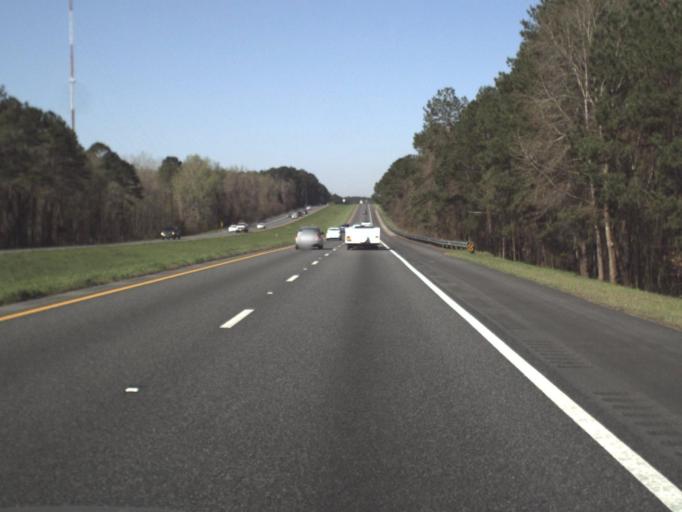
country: US
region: Florida
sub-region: Leon County
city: Tallahassee
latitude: 30.4985
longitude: -84.1935
